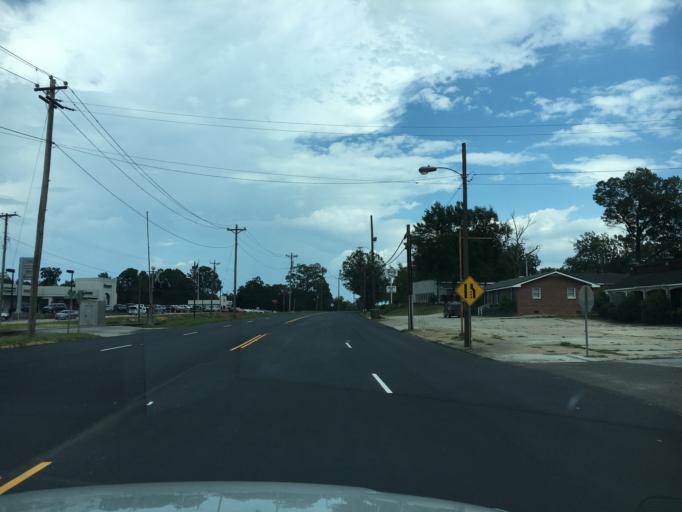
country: US
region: South Carolina
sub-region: Laurens County
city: Clinton
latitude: 34.4727
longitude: -81.8788
